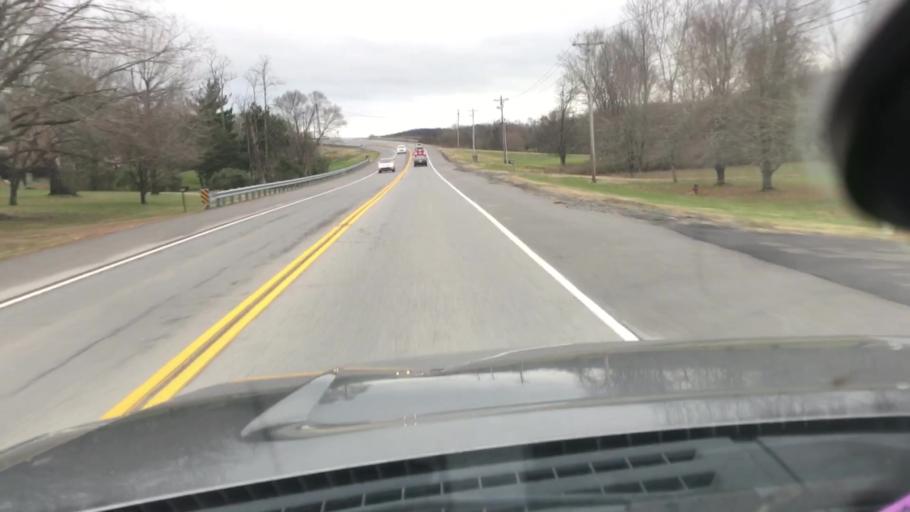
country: US
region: Tennessee
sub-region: Williamson County
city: Brentwood Estates
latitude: 35.9634
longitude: -86.7716
